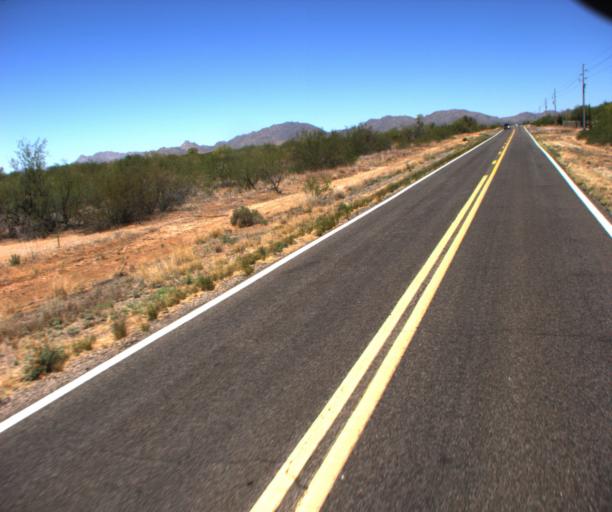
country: US
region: Arizona
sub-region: Yavapai County
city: Congress
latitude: 34.1159
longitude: -112.8347
